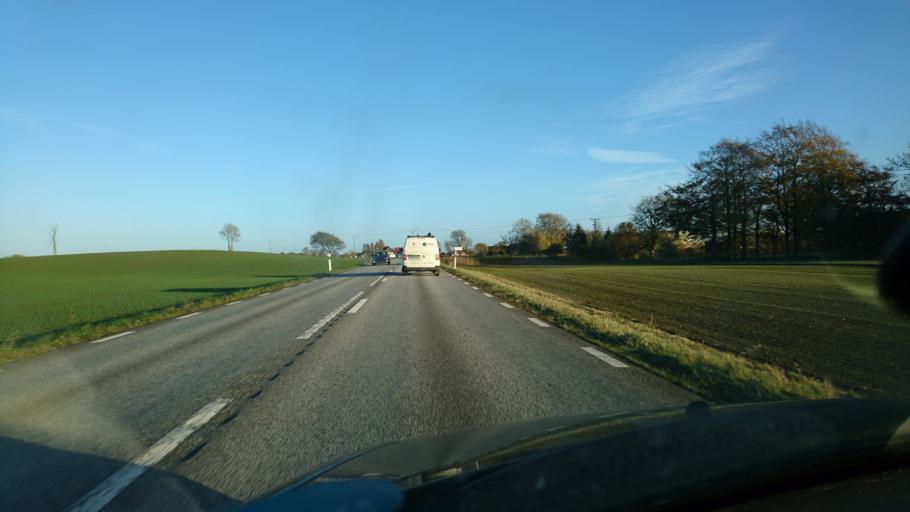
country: SE
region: Skane
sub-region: Tomelilla Kommun
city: Tomelilla
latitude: 55.5460
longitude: 14.0181
